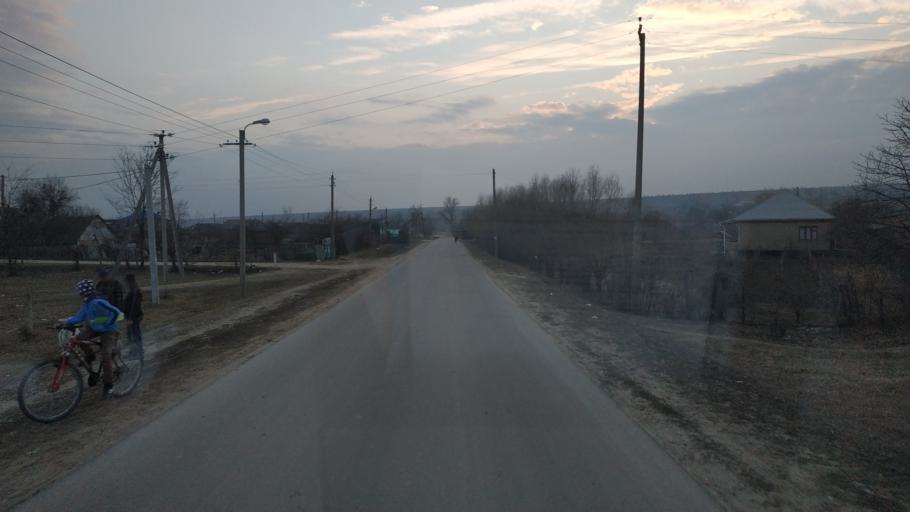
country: MD
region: Hincesti
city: Dancu
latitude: 46.6622
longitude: 28.3151
